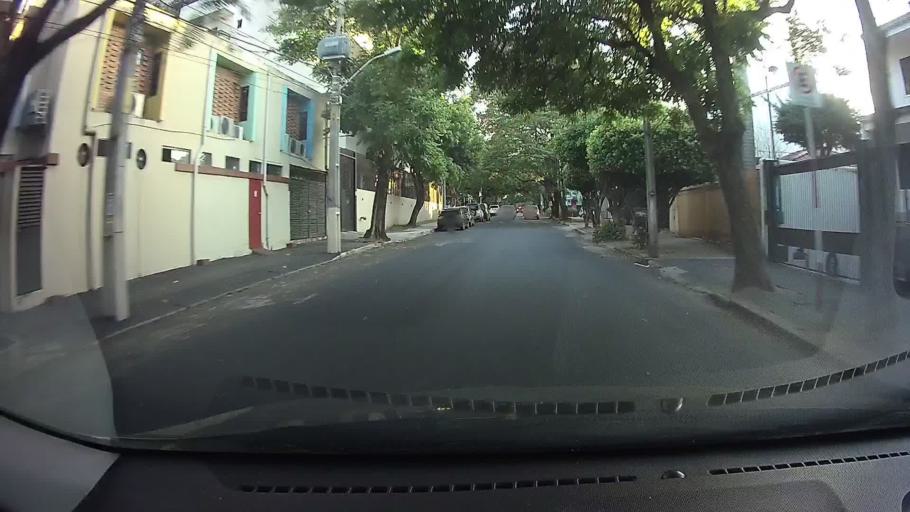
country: PY
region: Central
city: Lambare
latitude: -25.3074
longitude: -57.5777
